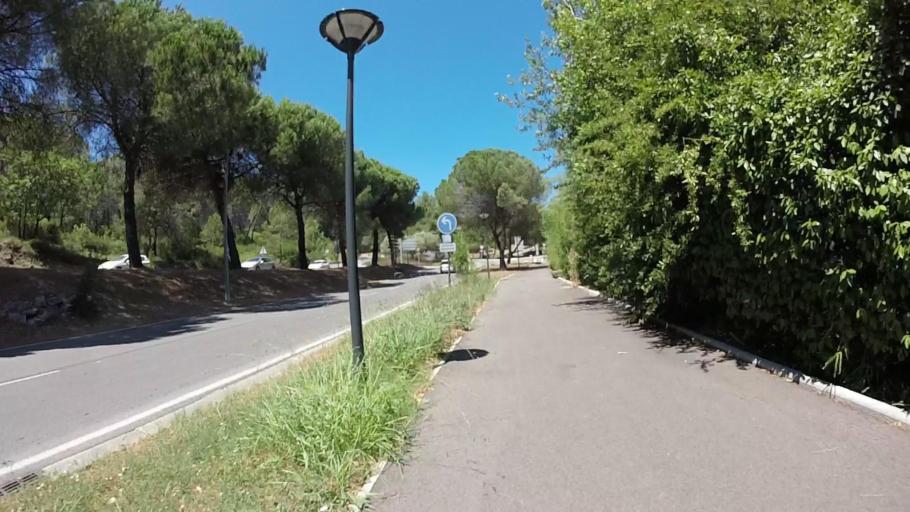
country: FR
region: Provence-Alpes-Cote d'Azur
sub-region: Departement des Alpes-Maritimes
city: Mougins
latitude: 43.6204
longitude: 7.0358
